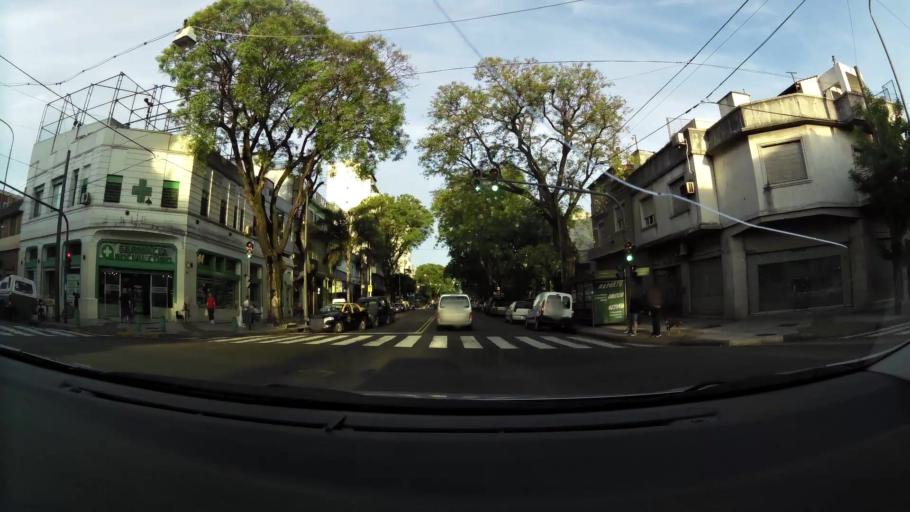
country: AR
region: Buenos Aires F.D.
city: Villa Lugano
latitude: -34.6418
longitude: -58.4324
